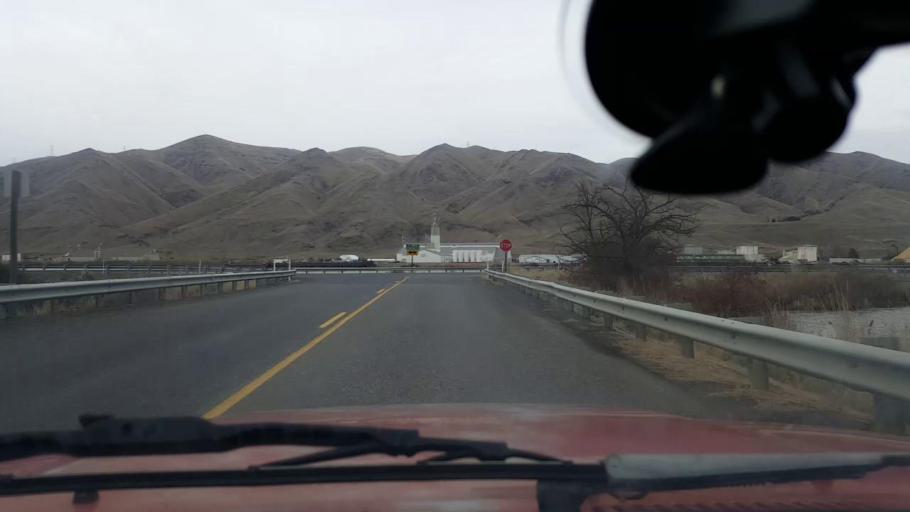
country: US
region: Washington
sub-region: Asotin County
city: Clarkston Heights-Vineland
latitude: 46.4192
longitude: -117.1145
